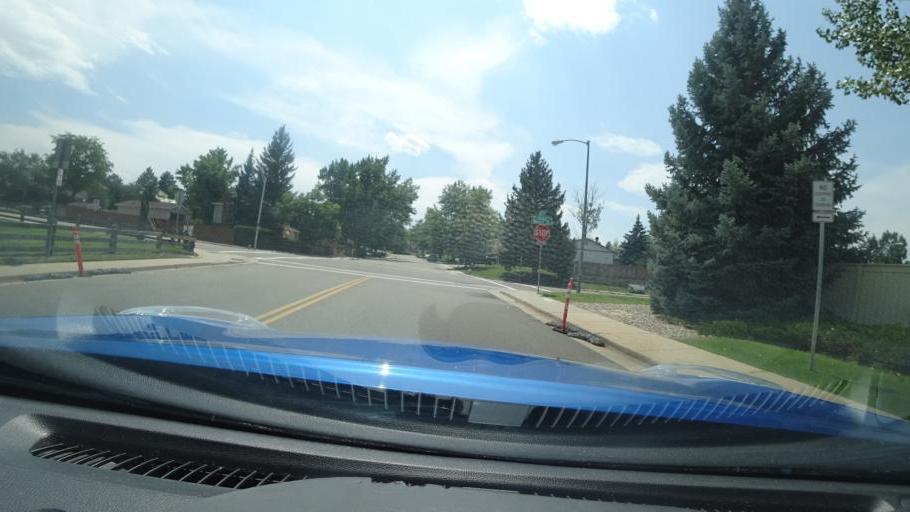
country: US
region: Colorado
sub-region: Adams County
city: Aurora
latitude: 39.6644
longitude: -104.7672
